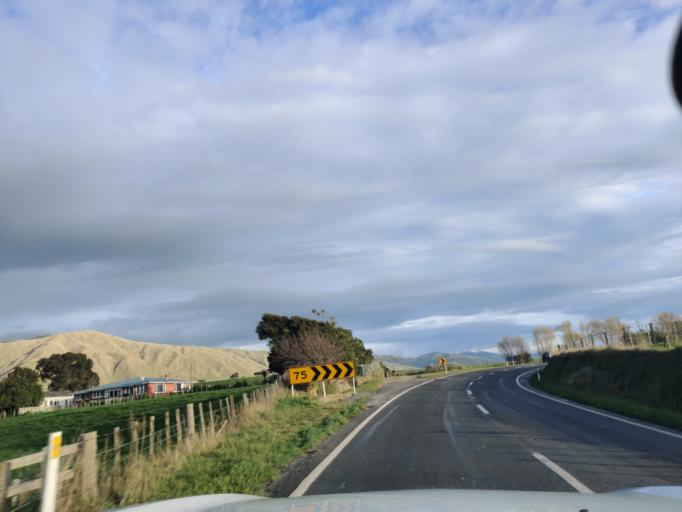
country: NZ
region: Manawatu-Wanganui
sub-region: Palmerston North City
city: Palmerston North
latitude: -40.4964
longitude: 175.4936
